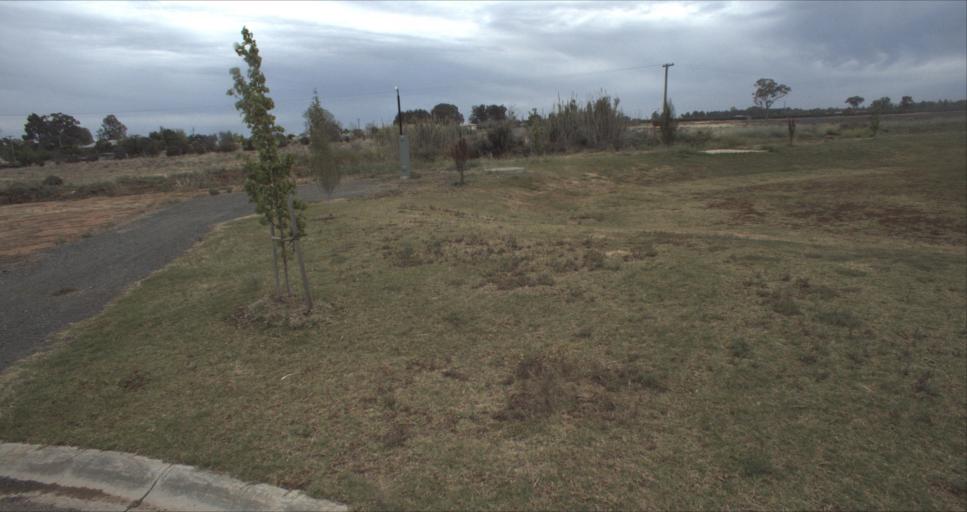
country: AU
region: New South Wales
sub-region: Leeton
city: Leeton
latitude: -34.5391
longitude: 146.3991
